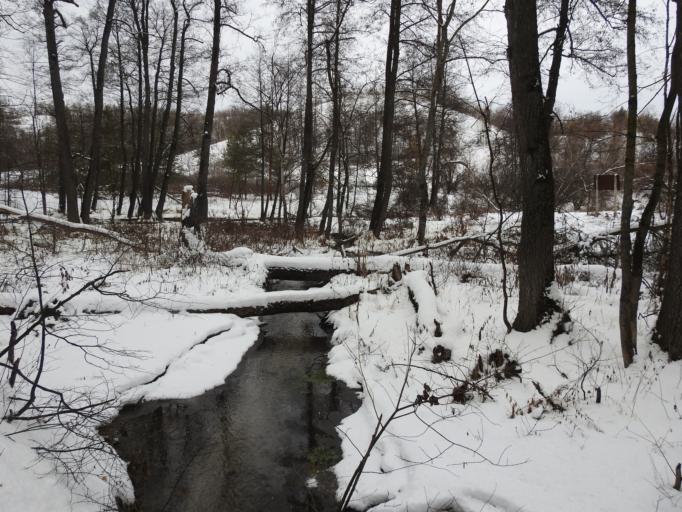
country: RU
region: Saratov
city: Tersa
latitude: 52.1079
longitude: 47.4717
